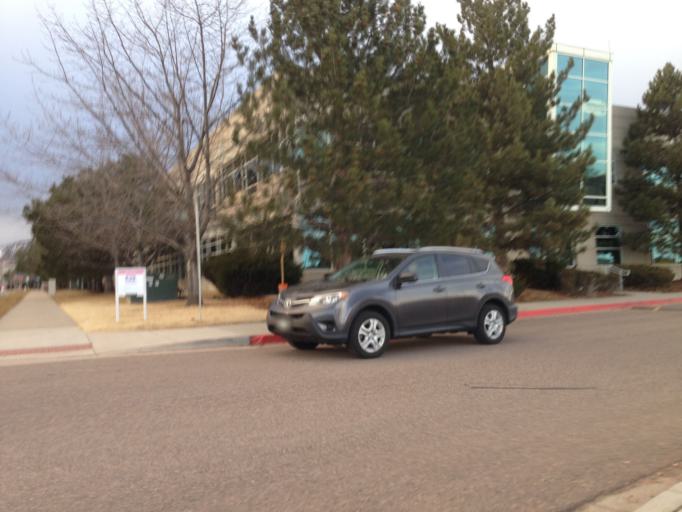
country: US
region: Colorado
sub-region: Boulder County
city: Boulder
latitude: 40.0198
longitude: -105.2479
